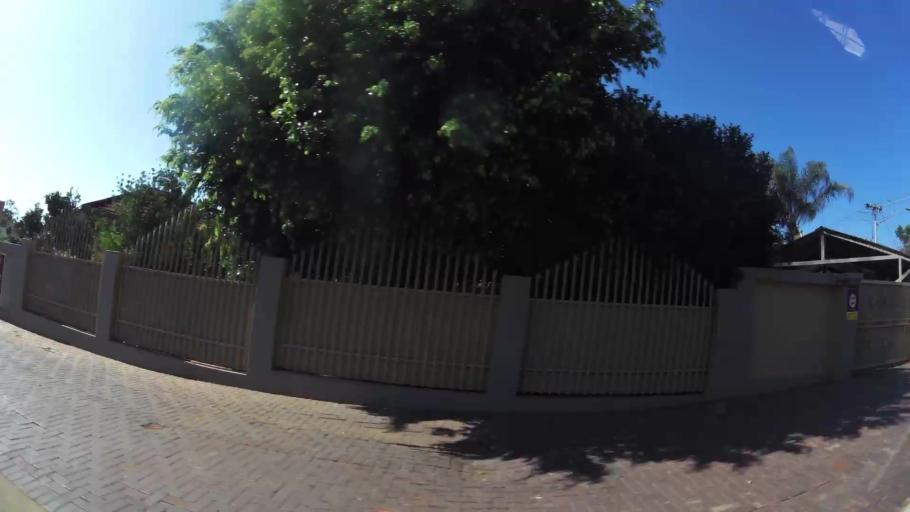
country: ZA
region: Gauteng
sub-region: City of Tshwane Metropolitan Municipality
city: Pretoria
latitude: -25.6848
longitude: 28.2226
